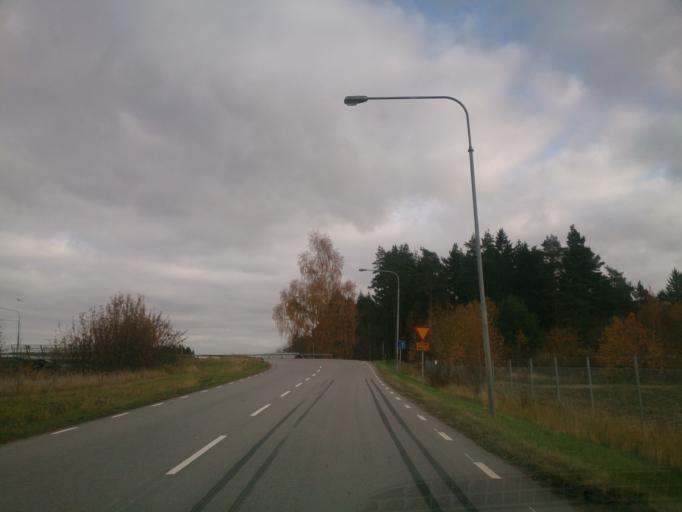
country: SE
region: OEstergoetland
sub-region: Linkopings Kommun
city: Linghem
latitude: 58.4379
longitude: 15.7997
